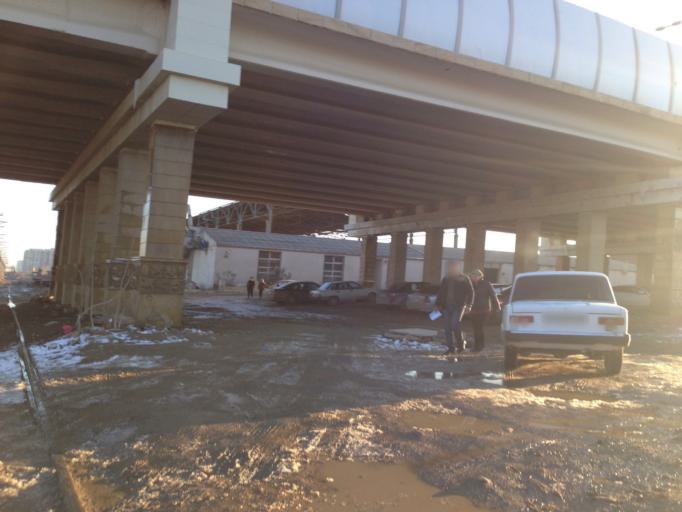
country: AZ
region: Baki
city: Baku
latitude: 40.4202
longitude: 49.8675
